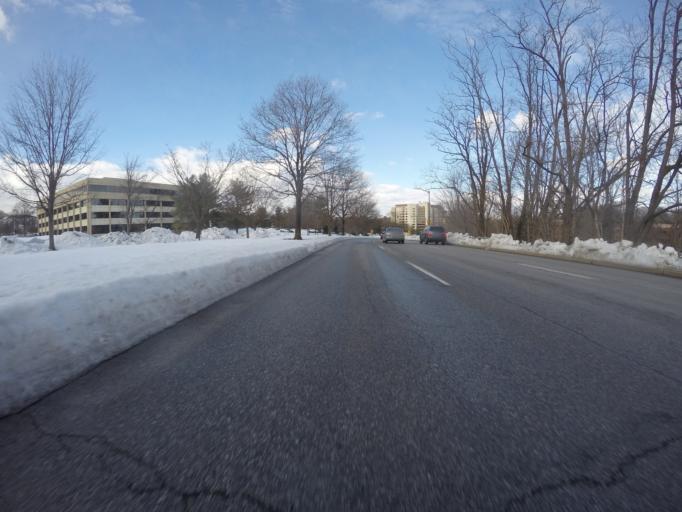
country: US
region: Maryland
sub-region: Howard County
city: Columbia
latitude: 39.2187
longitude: -76.8583
